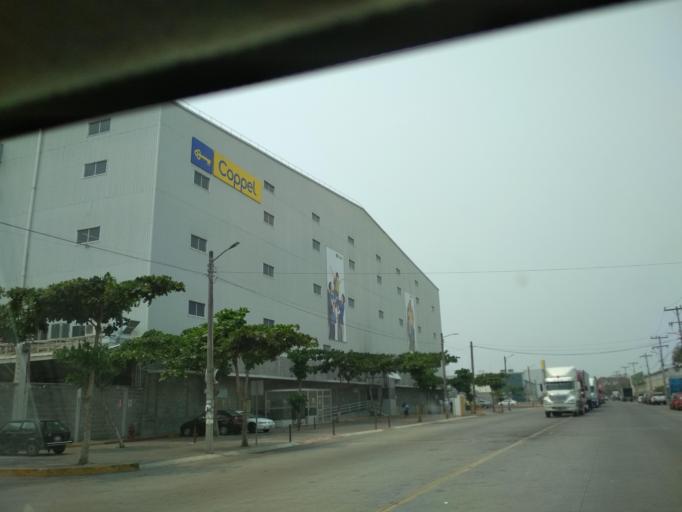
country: MX
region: Veracruz
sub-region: Veracruz
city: Las Amapolas
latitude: 19.1653
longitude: -96.2258
